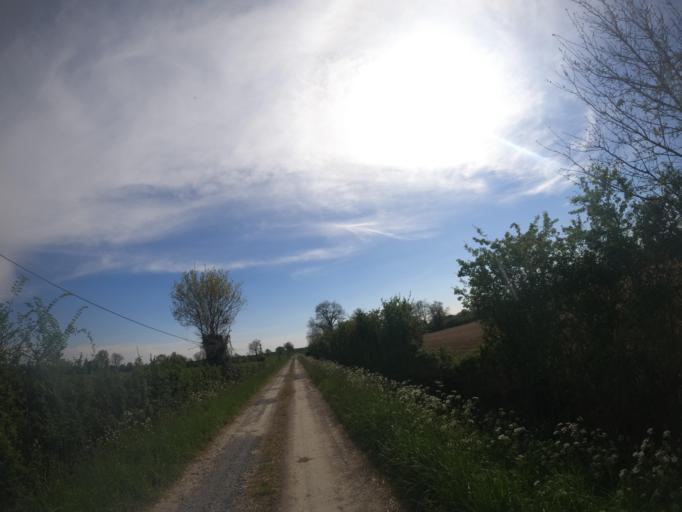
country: FR
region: Poitou-Charentes
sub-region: Departement des Deux-Sevres
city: Saint-Varent
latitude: 46.9210
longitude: -0.2424
